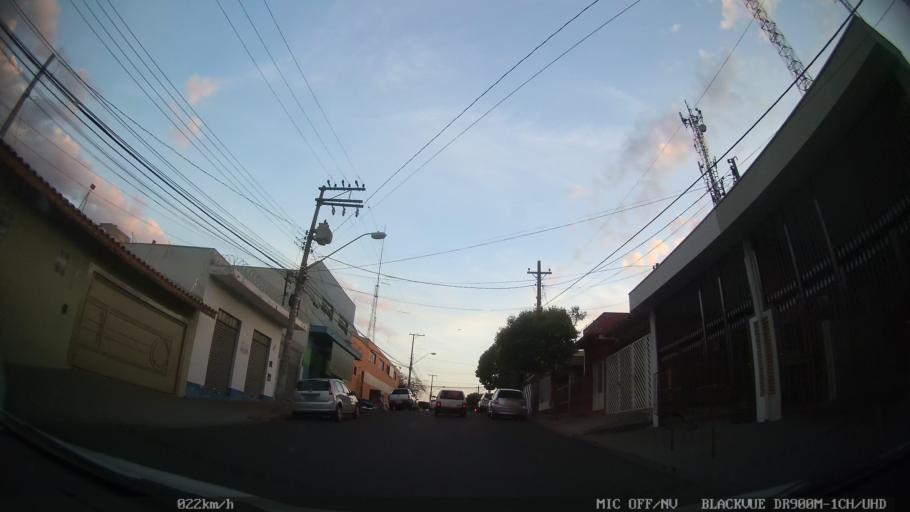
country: BR
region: Sao Paulo
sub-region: Ribeirao Preto
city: Ribeirao Preto
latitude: -21.1535
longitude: -47.8291
